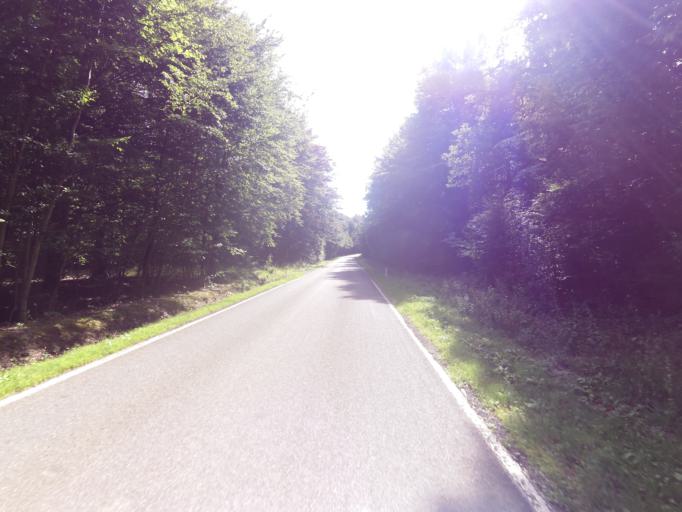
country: BE
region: Wallonia
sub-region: Province du Luxembourg
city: Nassogne
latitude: 50.0755
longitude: 5.3460
